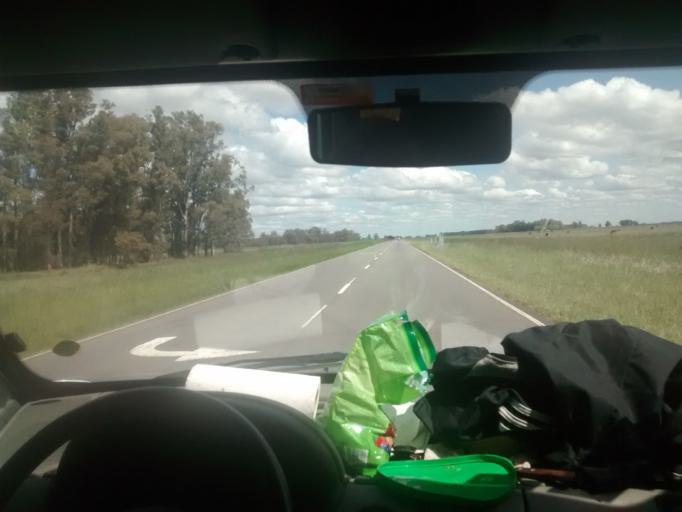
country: AR
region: Buenos Aires
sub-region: Partido de Rauch
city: Rauch
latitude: -36.5605
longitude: -58.5602
